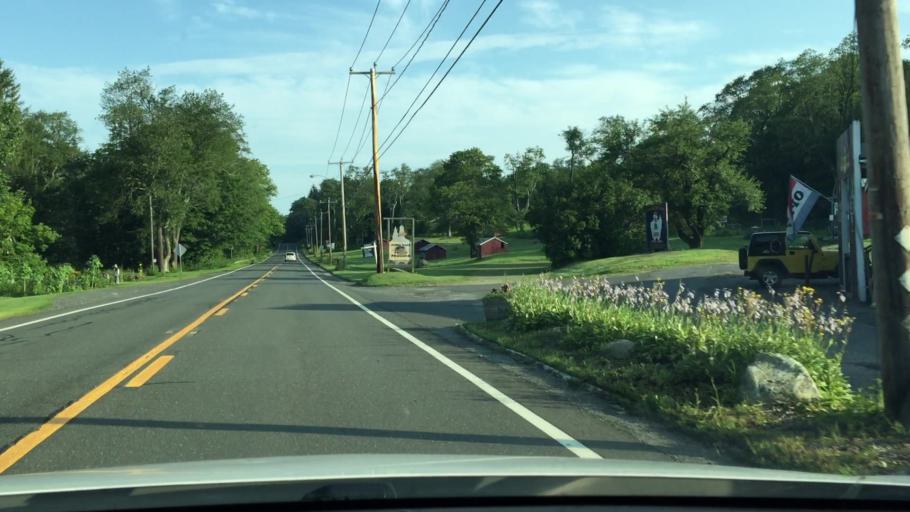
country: US
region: Massachusetts
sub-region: Berkshire County
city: Otis
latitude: 42.2326
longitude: -73.1103
